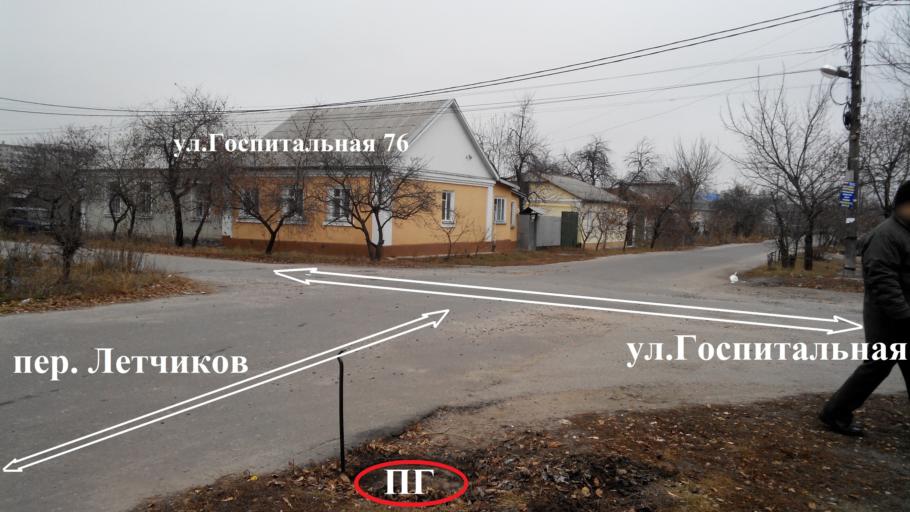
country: RU
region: Voronezj
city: Voronezh
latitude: 51.6381
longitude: 39.1696
